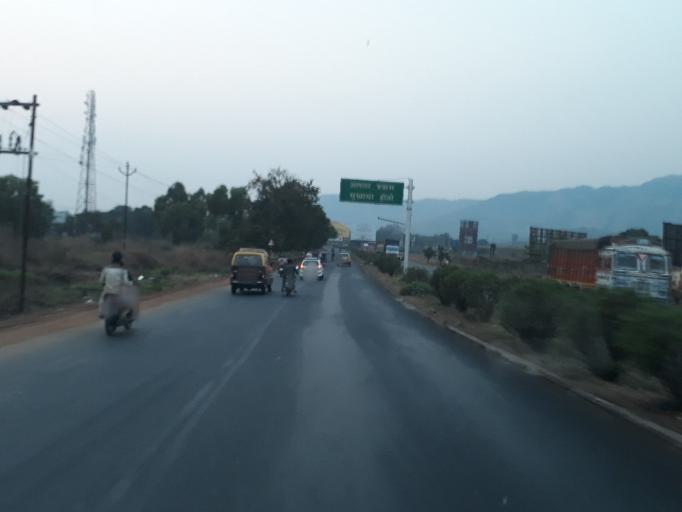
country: IN
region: Maharashtra
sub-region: Raigarh
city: Karjat
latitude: 18.8979
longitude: 73.2509
